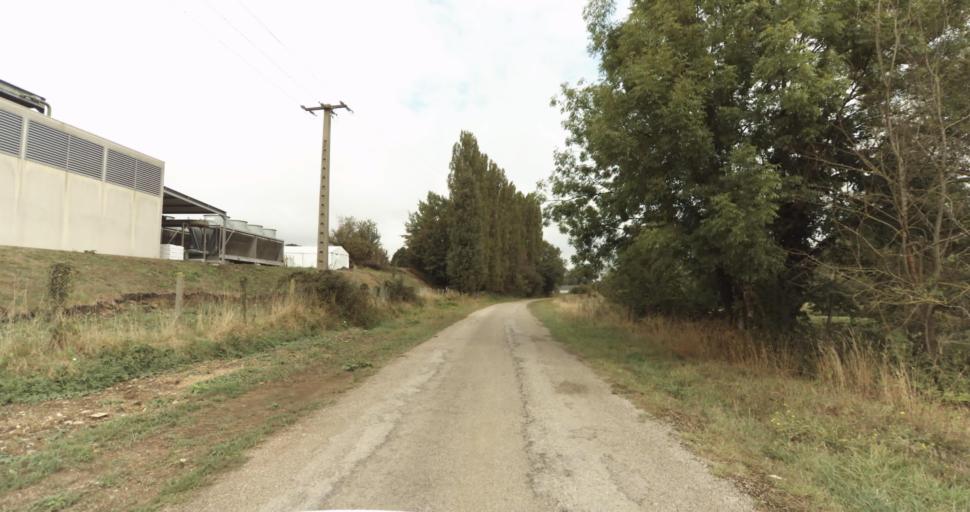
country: FR
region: Lower Normandy
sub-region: Departement de l'Orne
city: Vimoutiers
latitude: 48.9351
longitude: 0.1922
